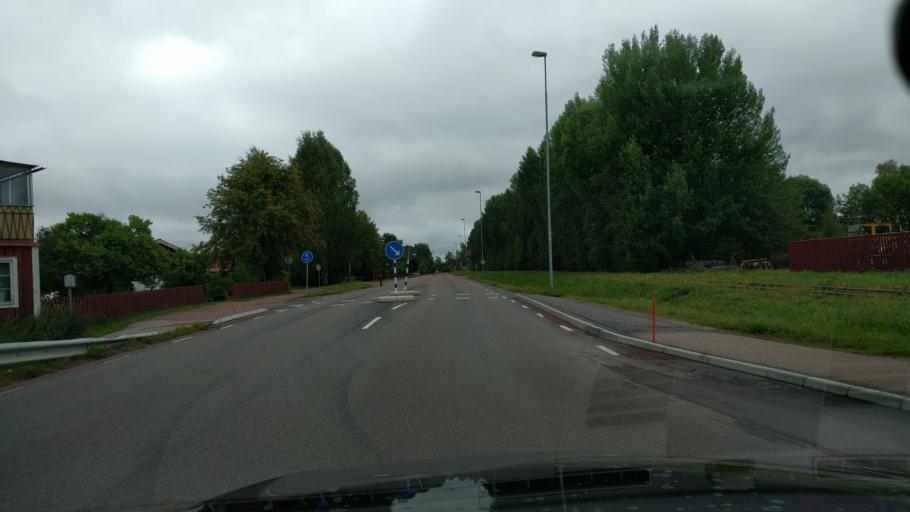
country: SE
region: Dalarna
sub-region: Mora Kommun
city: Mora
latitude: 61.0053
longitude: 14.5231
